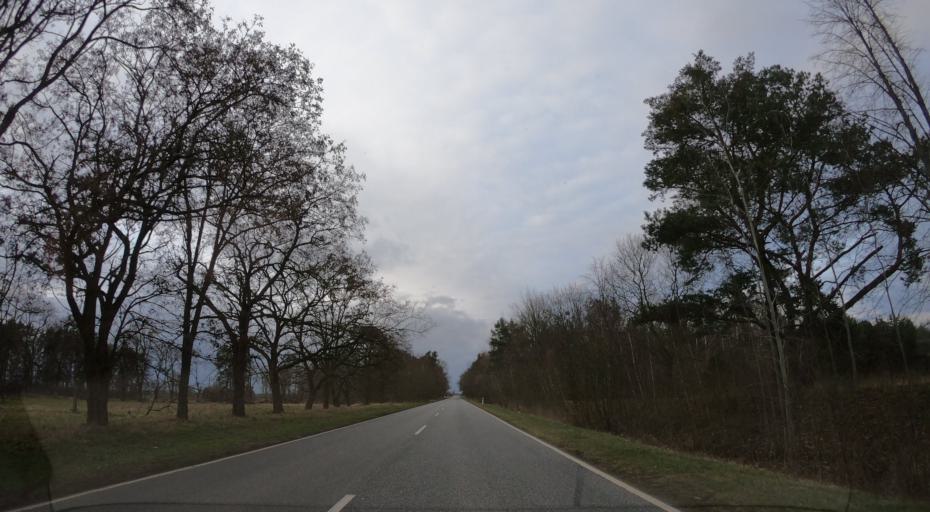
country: PL
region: West Pomeranian Voivodeship
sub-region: Powiat pyrzycki
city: Lipiany
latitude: 52.9384
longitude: 14.9528
